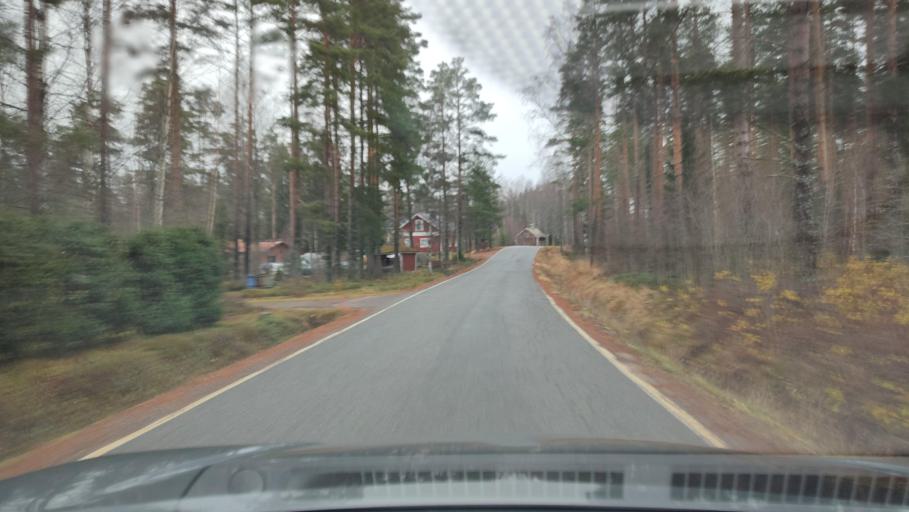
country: FI
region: Southern Ostrobothnia
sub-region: Suupohja
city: Isojoki
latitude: 62.1586
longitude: 21.8818
